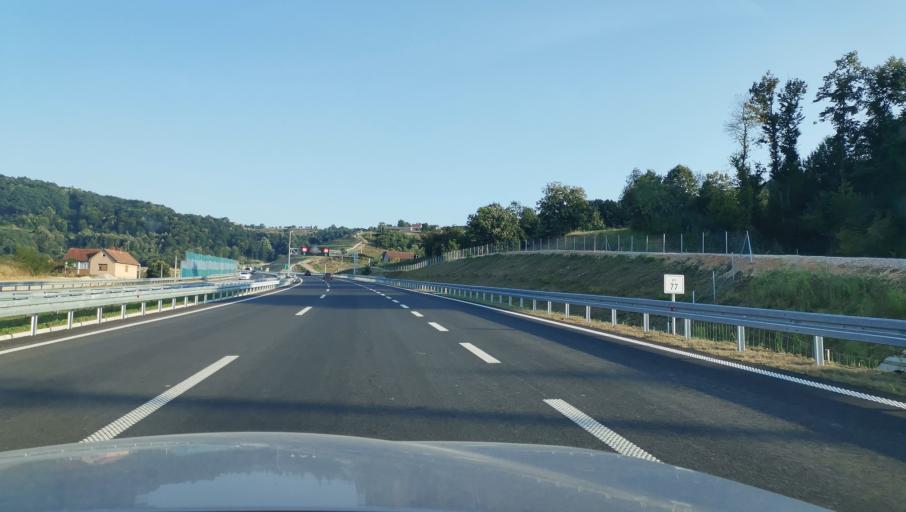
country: RS
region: Central Serbia
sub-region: Kolubarski Okrug
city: Ljig
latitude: 44.2190
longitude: 20.2567
